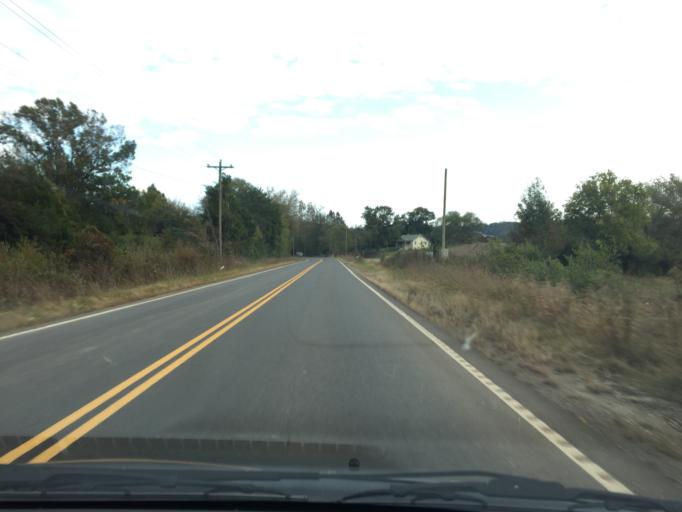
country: US
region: Tennessee
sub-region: Monroe County
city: Sweetwater
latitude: 35.6267
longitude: -84.5005
